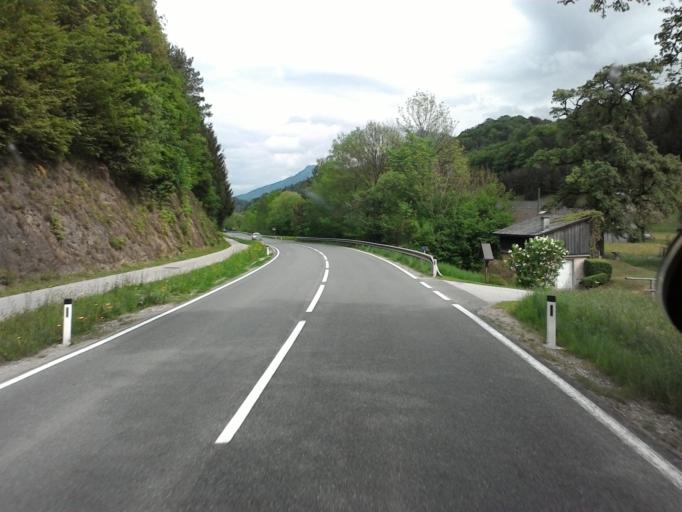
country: AT
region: Upper Austria
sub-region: Politischer Bezirk Kirchdorf an der Krems
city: Micheldorf in Oberoesterreich
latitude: 47.8506
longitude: 14.1564
